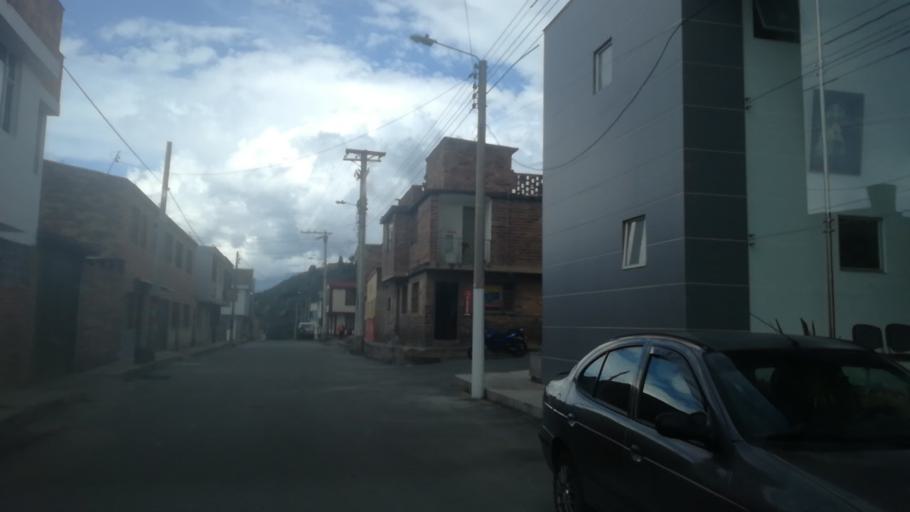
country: CO
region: Boyaca
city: Socha Viejo
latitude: 5.9979
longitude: -72.6899
